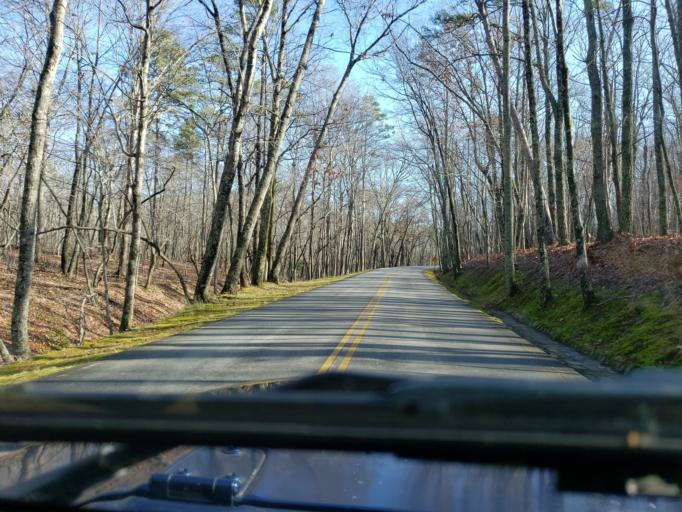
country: US
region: North Carolina
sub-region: Cleveland County
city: White Plains
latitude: 35.1486
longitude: -81.3892
